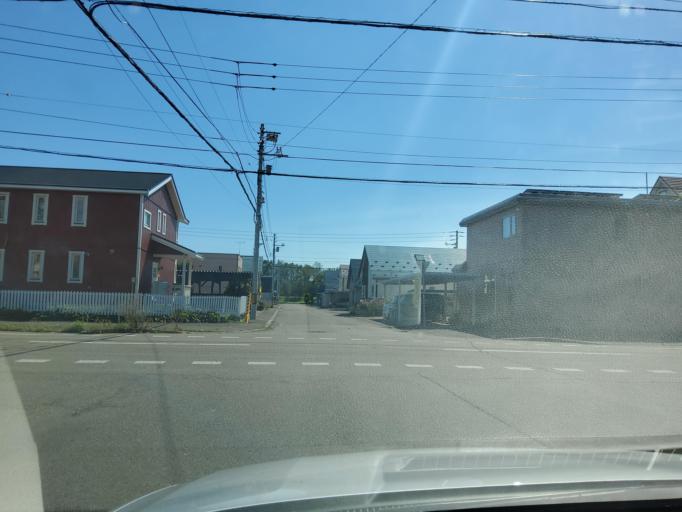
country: JP
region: Hokkaido
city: Obihiro
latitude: 42.9409
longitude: 143.2200
